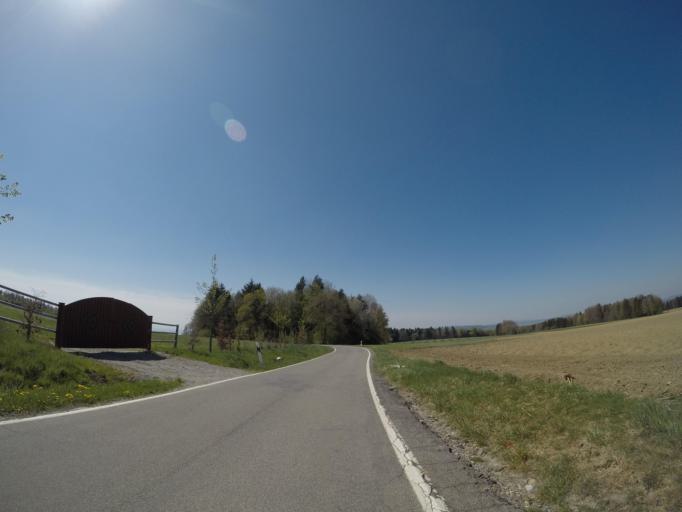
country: DE
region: Baden-Wuerttemberg
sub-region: Tuebingen Region
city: Markdorf
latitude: 47.7451
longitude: 9.3859
